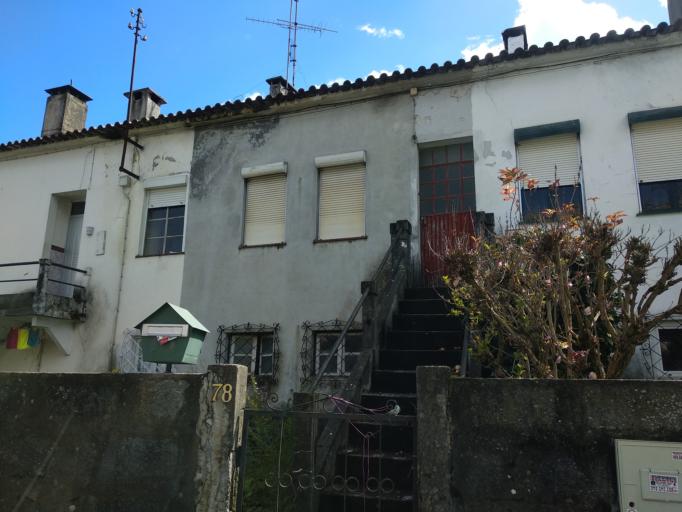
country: PT
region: Braga
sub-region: Braga
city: Braga
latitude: 41.5651
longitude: -8.4088
